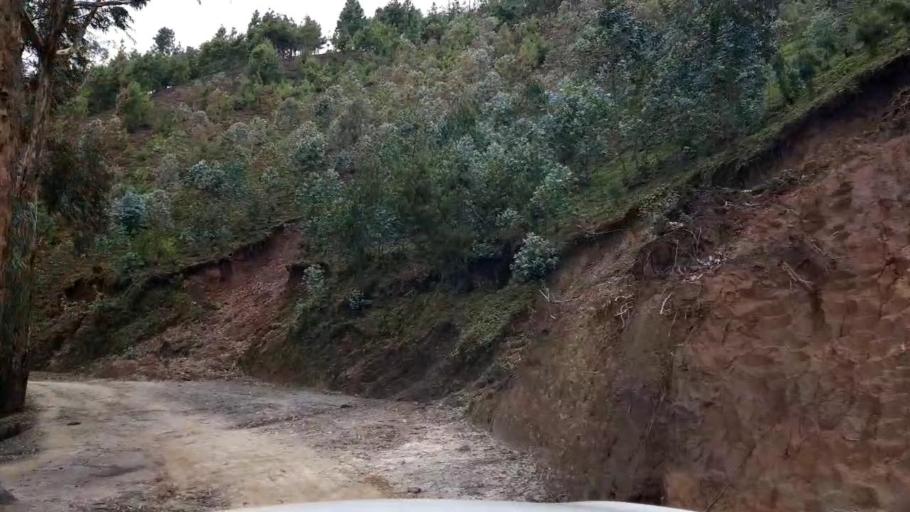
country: RW
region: Western Province
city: Kibuye
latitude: -1.9584
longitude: 29.4765
